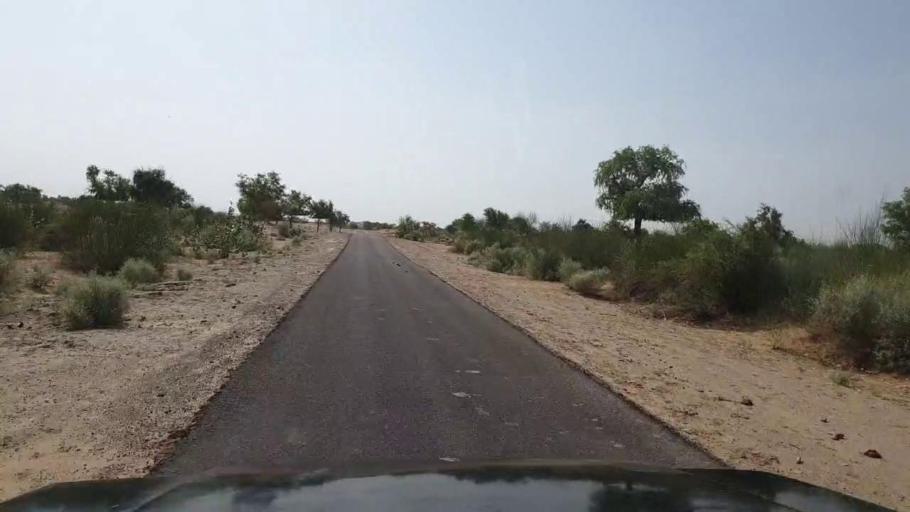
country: PK
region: Sindh
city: Islamkot
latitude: 24.9410
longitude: 70.0766
